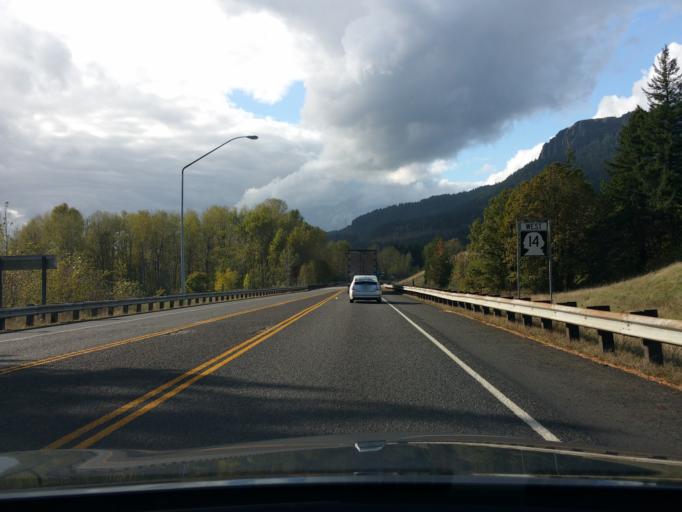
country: US
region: Oregon
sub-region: Hood River County
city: Cascade Locks
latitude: 45.6406
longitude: -121.9756
